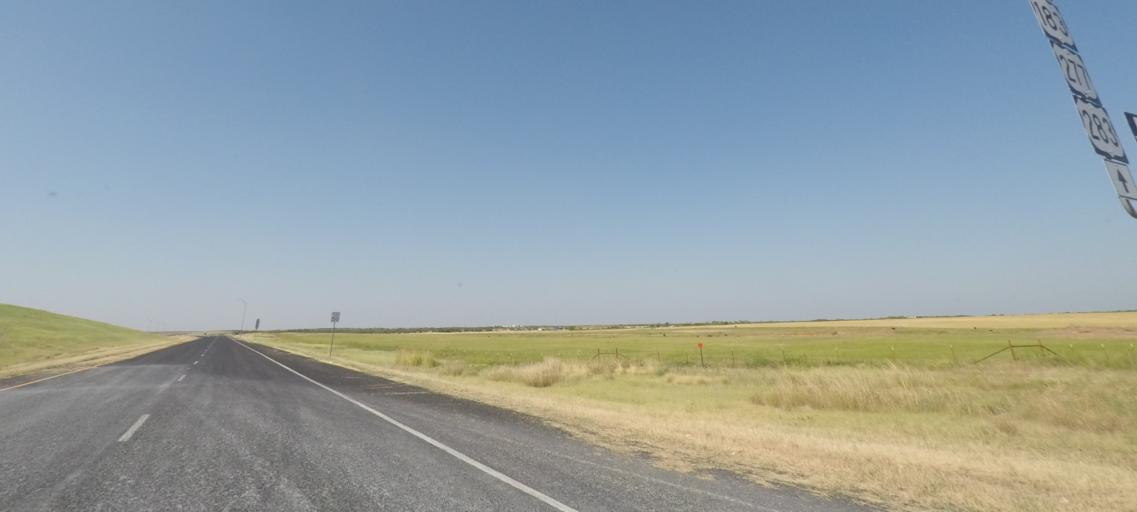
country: US
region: Texas
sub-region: Baylor County
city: Seymour
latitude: 33.5959
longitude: -99.2407
